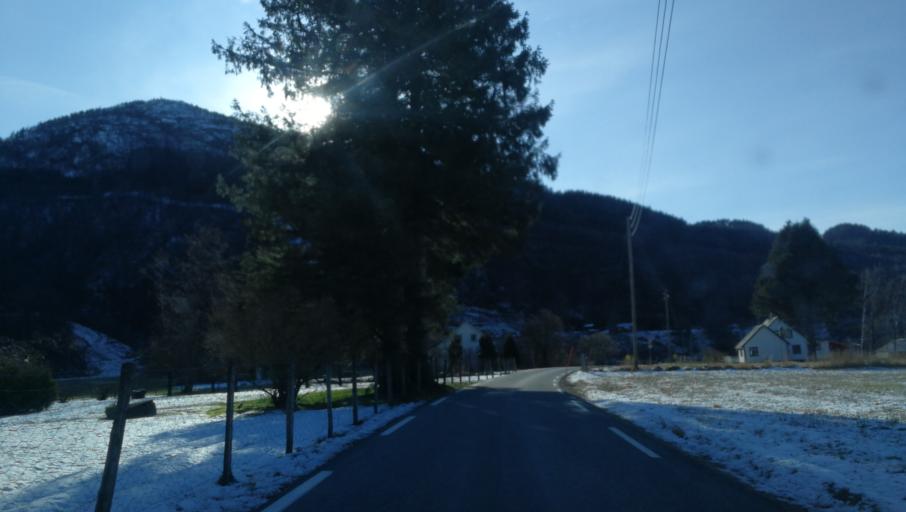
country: NO
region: Rogaland
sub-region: Hjelmeland
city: Hjelmelandsvagen
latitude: 59.1293
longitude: 6.2726
